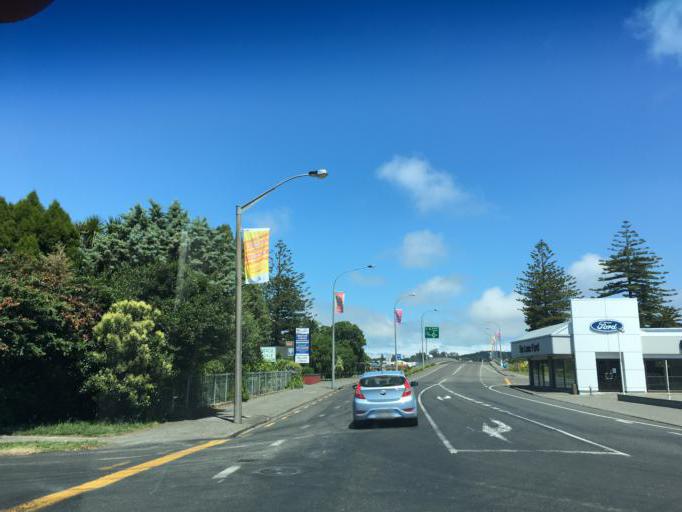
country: NZ
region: Hawke's Bay
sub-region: Wairoa District
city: Wairoa
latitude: -39.0296
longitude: 177.4191
